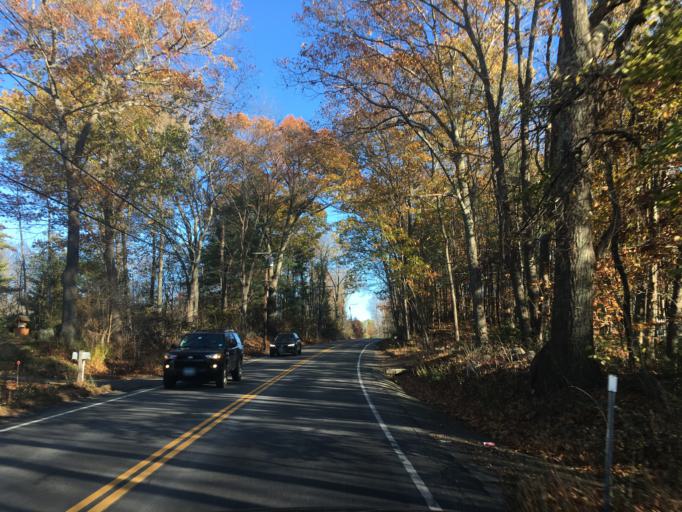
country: US
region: New Hampshire
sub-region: Rockingham County
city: Stratham Station
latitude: 43.0389
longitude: -70.9062
